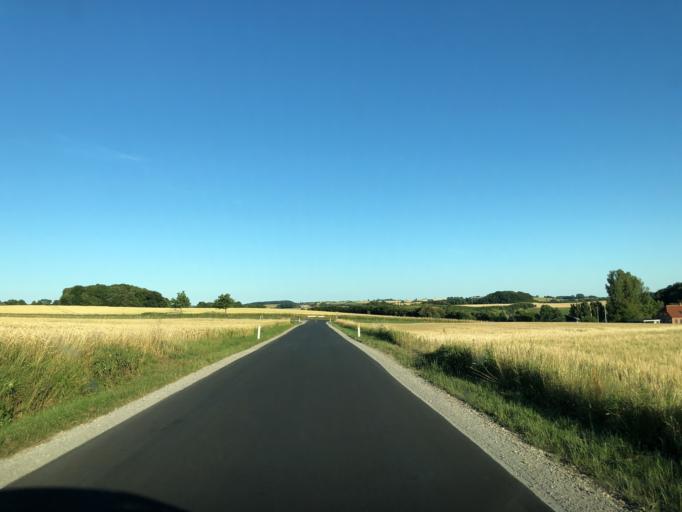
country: DK
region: Central Jutland
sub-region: Horsens Kommune
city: Horsens
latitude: 55.9481
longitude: 9.8543
